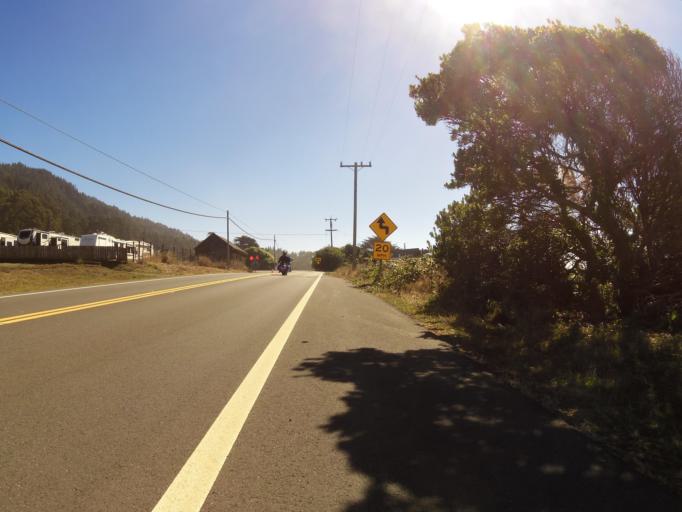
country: US
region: California
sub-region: Mendocino County
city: Fort Bragg
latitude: 39.6367
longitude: -123.7849
